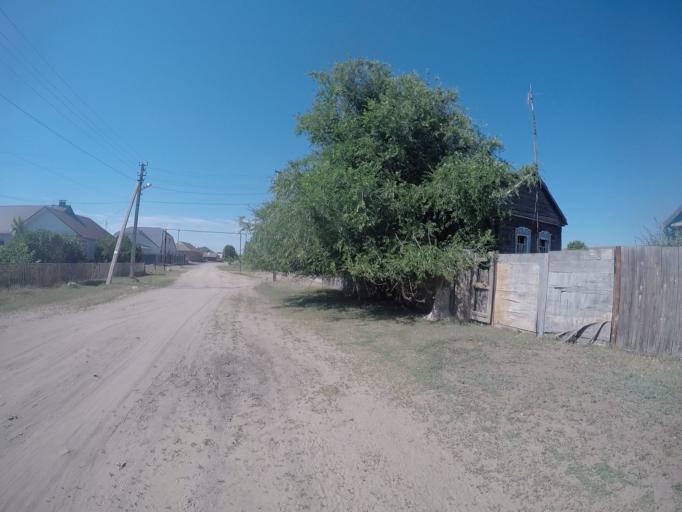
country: RU
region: Saratov
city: Privolzhskiy
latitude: 51.1830
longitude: 45.9167
